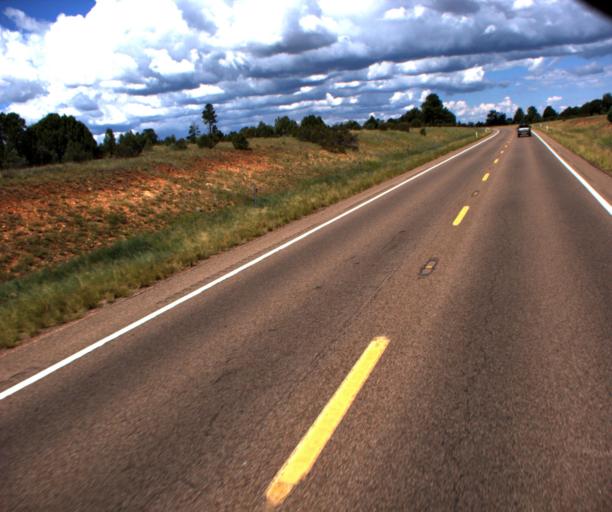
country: US
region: Arizona
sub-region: Navajo County
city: Heber-Overgaard
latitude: 34.3774
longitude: -110.4665
